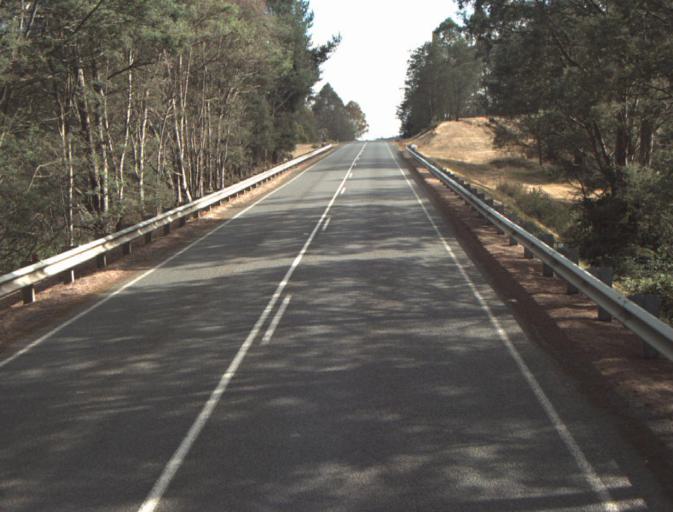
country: AU
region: Tasmania
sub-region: Launceston
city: Mayfield
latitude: -41.2881
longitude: 147.2176
